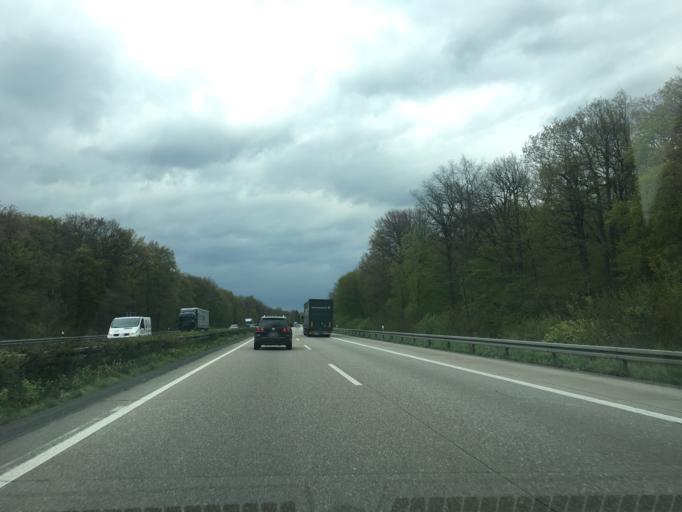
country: DE
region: North Rhine-Westphalia
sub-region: Regierungsbezirk Munster
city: Ascheberg
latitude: 51.8502
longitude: 7.5803
